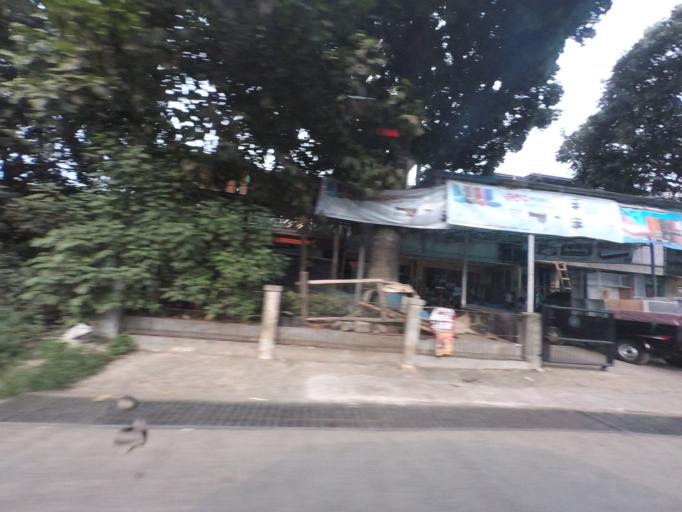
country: ID
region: West Java
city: Cicurug
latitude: -6.7625
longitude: 106.8013
